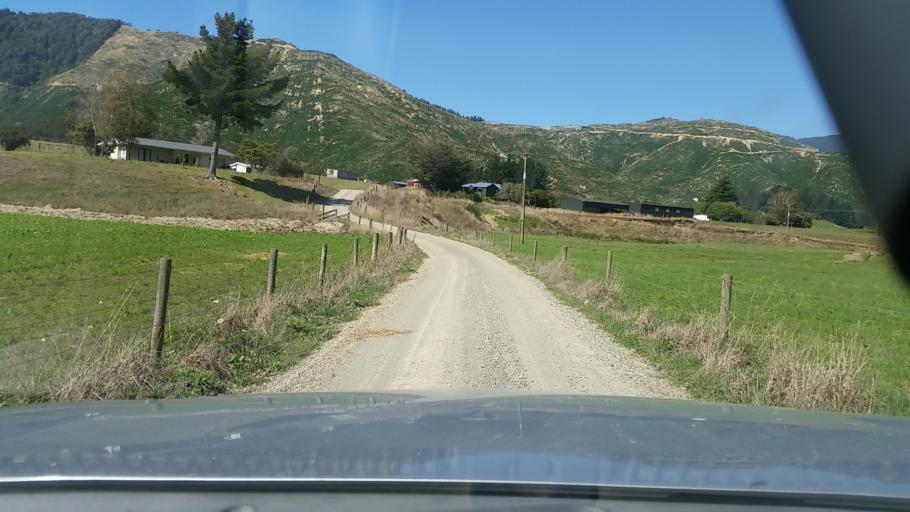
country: NZ
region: Nelson
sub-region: Nelson City
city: Nelson
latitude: -41.2706
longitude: 173.5786
